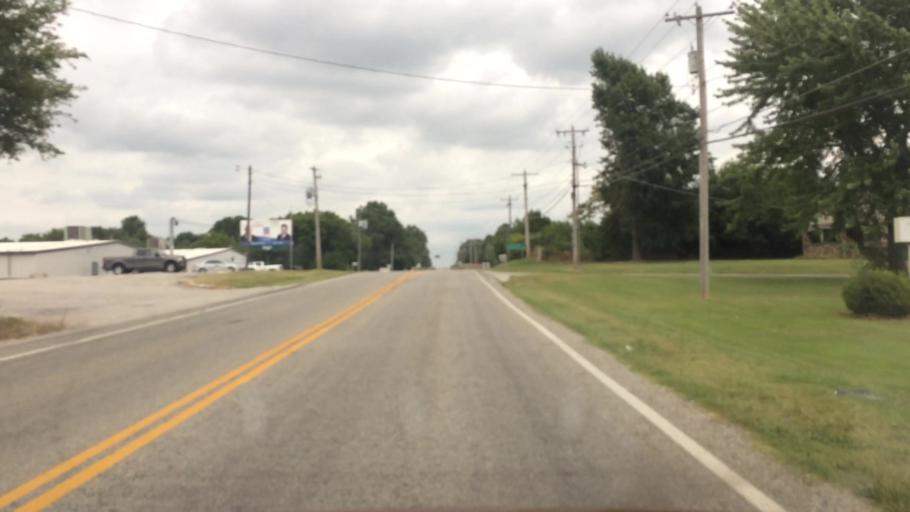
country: US
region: Missouri
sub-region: Greene County
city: Springfield
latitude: 37.2936
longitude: -93.2637
